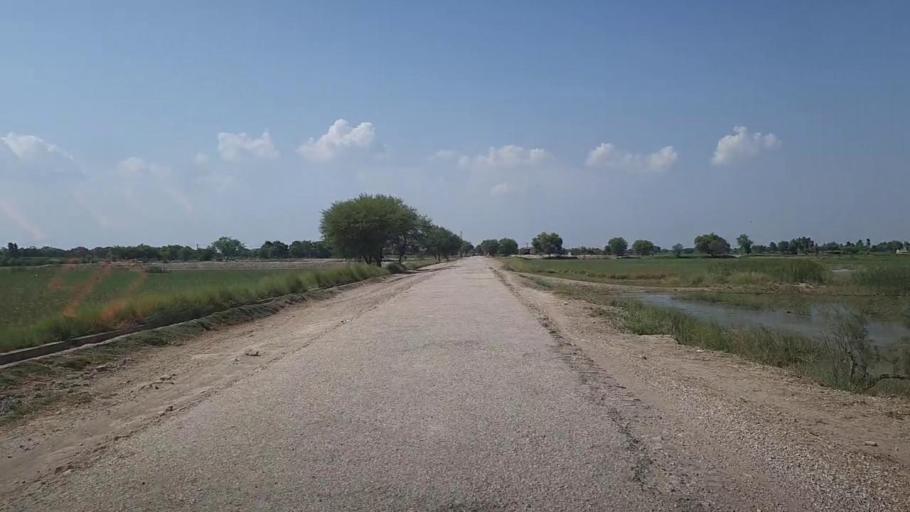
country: PK
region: Sindh
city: Khairpur
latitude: 28.1101
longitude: 69.6209
